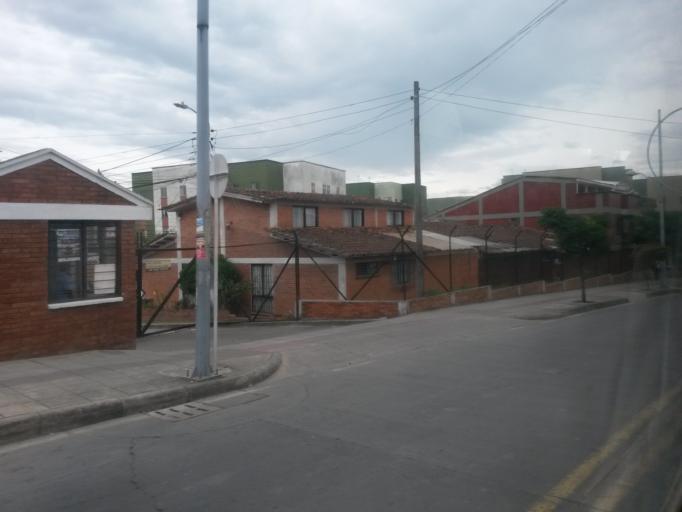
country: CO
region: Cauca
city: Popayan
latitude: 2.4577
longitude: -76.5922
